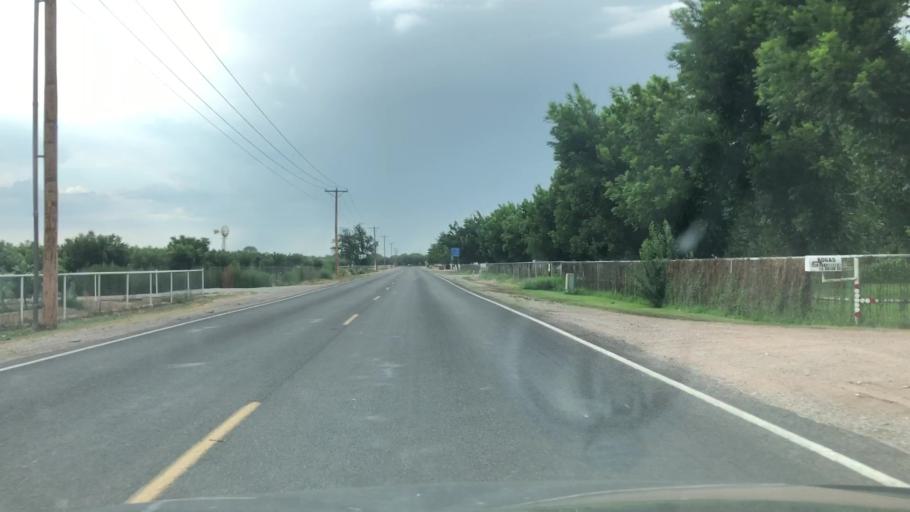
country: US
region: Texas
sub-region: El Paso County
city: Canutillo
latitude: 31.9271
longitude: -106.6284
